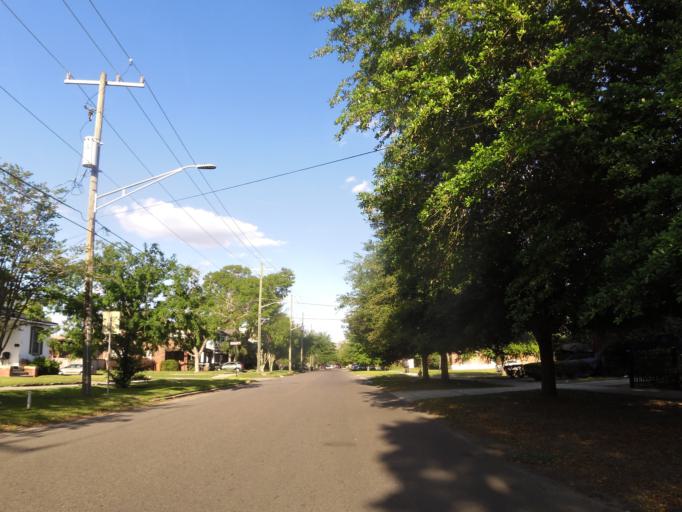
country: US
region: Florida
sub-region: Duval County
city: Jacksonville
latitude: 30.3156
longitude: -81.6863
